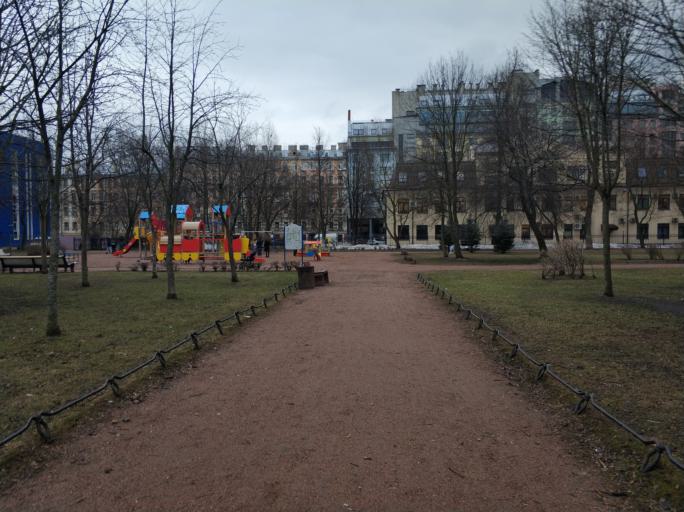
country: RU
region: Leningrad
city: Finlyandskiy
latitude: 59.9683
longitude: 30.3475
